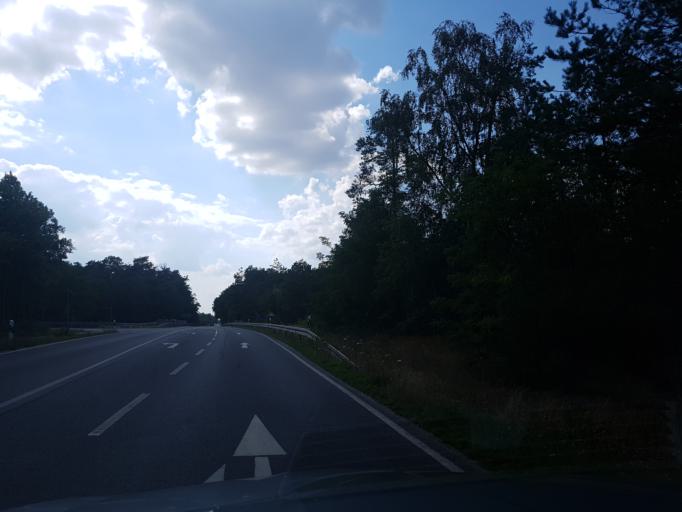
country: DE
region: Brandenburg
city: Schonewalde
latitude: 51.6348
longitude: 13.6372
